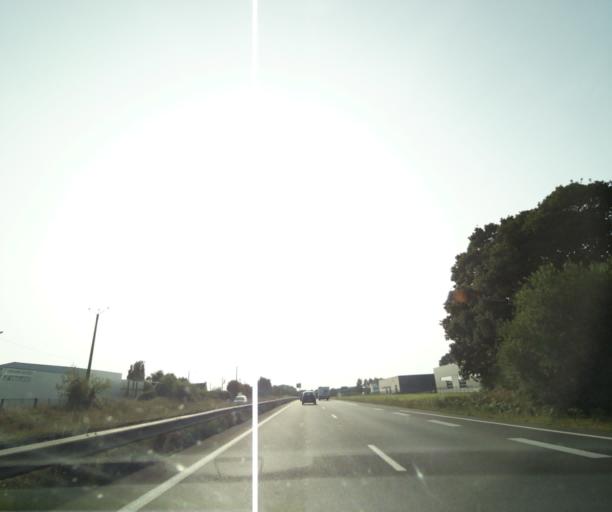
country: FR
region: Brittany
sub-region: Departement des Cotes-d'Armor
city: Plouagat
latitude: 48.5298
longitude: -2.9738
